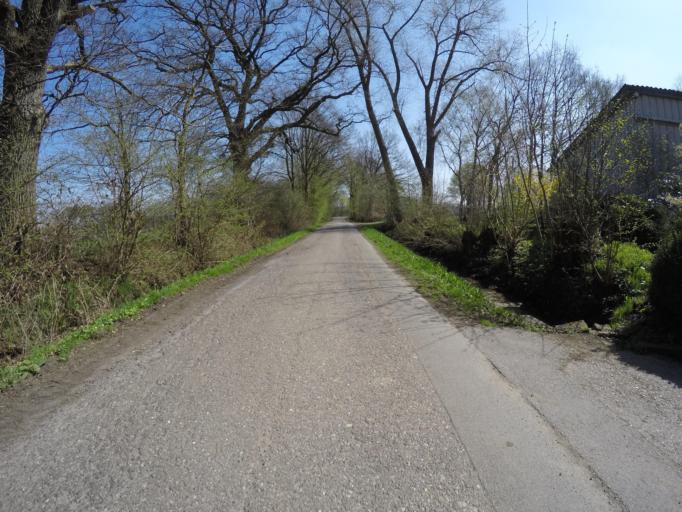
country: DE
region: Schleswig-Holstein
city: Ellerau
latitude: 53.7453
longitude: 9.9085
